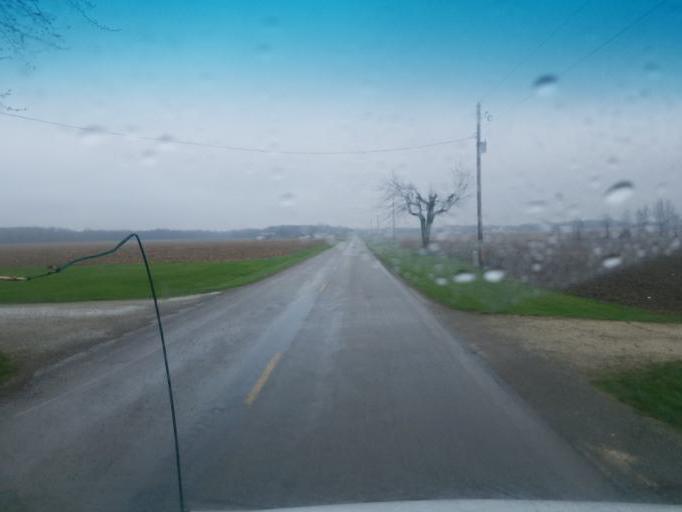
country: US
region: Ohio
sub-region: Wyandot County
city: Carey
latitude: 40.9854
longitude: -83.2834
